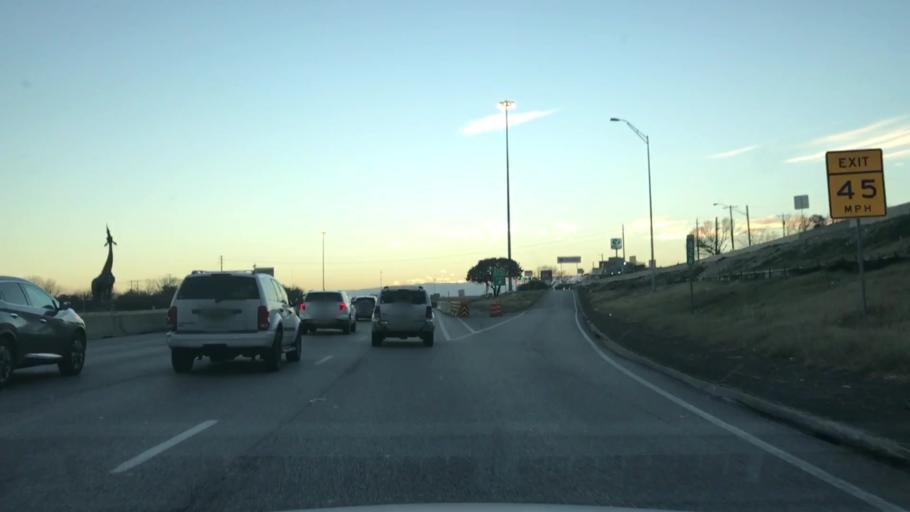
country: US
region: Texas
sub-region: Dallas County
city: Dallas
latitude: 32.7452
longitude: -96.8131
